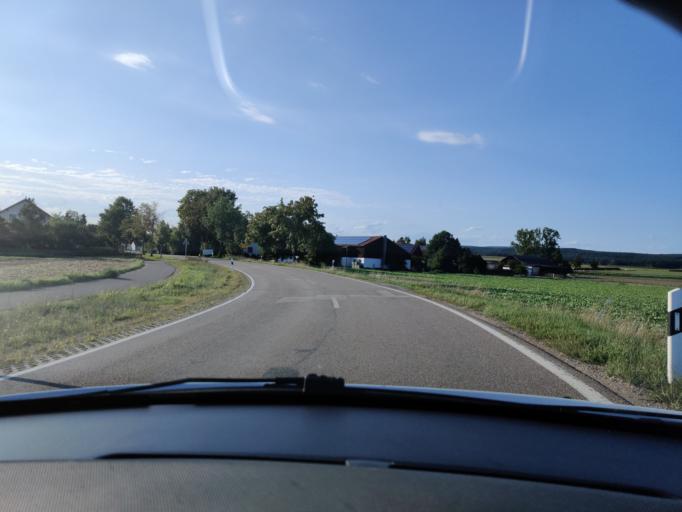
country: DE
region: Bavaria
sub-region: Upper Palatinate
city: Stulln
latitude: 49.4127
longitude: 12.1263
